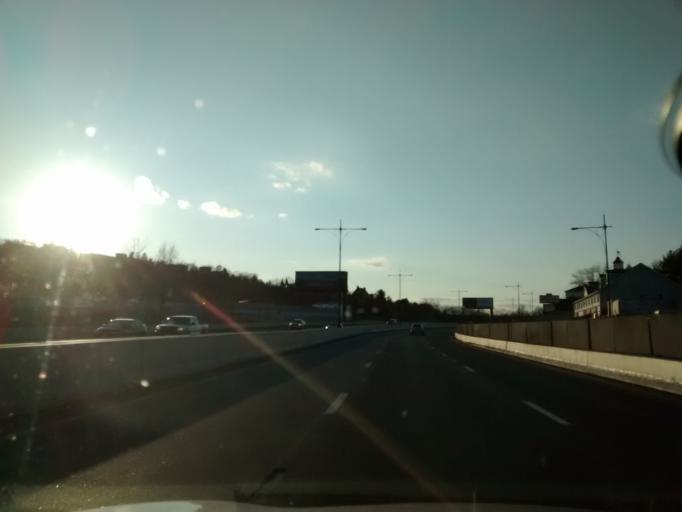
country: US
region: Massachusetts
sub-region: Worcester County
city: Worcester
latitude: 42.2376
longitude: -71.7966
